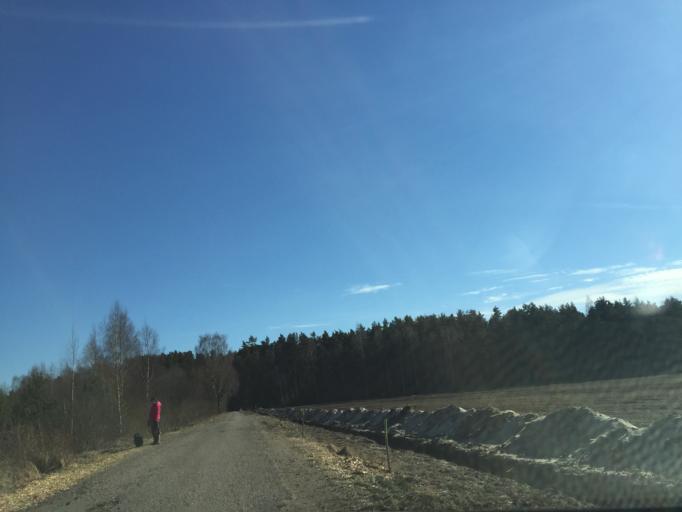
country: LV
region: Babite
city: Pinki
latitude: 56.9709
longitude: 23.9841
